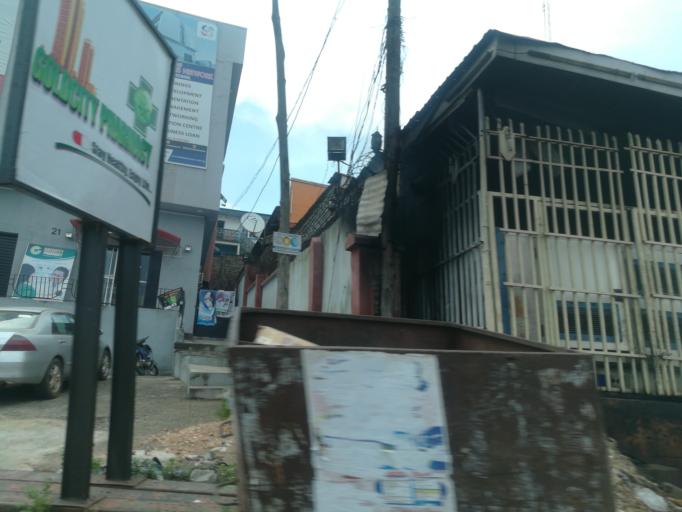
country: NG
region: Oyo
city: Ibadan
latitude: 7.4129
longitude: 3.8948
